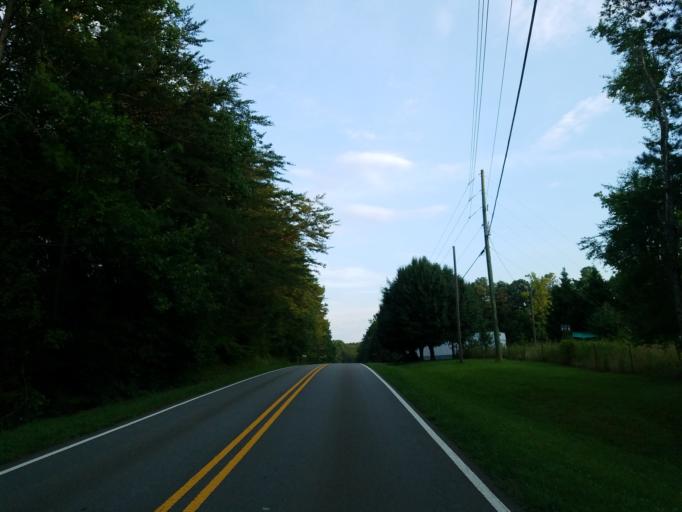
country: US
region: Georgia
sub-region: Pickens County
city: Jasper
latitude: 34.5557
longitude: -84.4700
